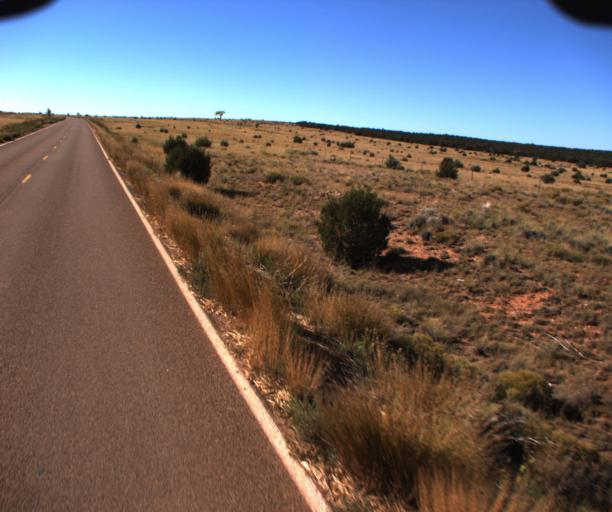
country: US
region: Arizona
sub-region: Navajo County
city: Heber-Overgaard
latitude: 34.4913
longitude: -110.3407
